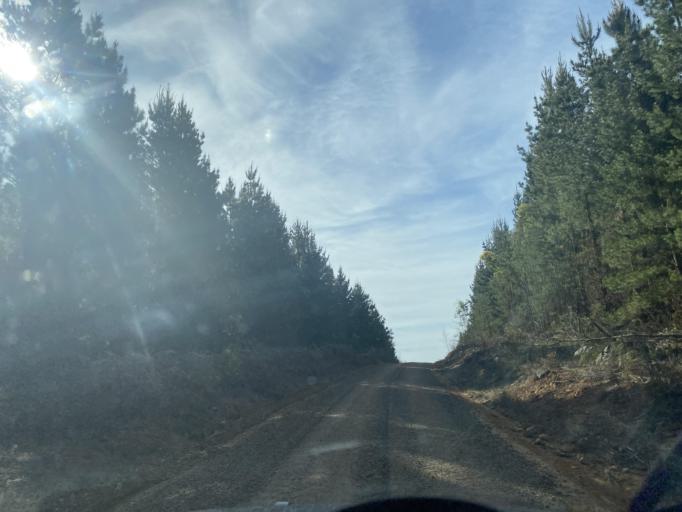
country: AU
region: Victoria
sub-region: Mansfield
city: Mansfield
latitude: -36.8755
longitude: 146.1842
